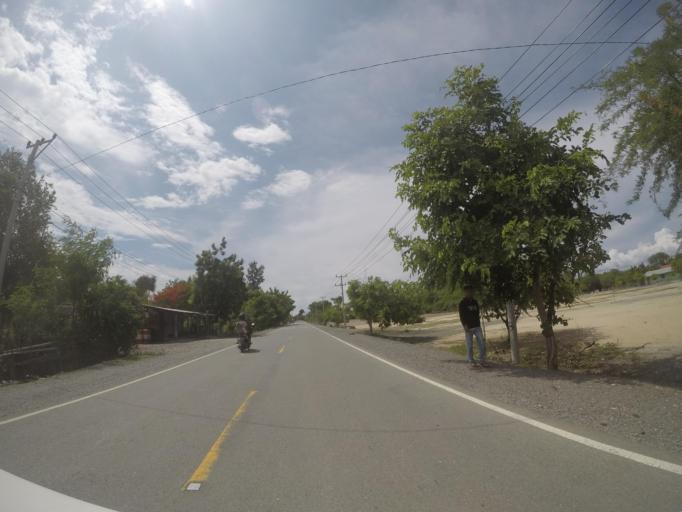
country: TL
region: Liquica
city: Liquica
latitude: -8.5653
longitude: 125.4197
